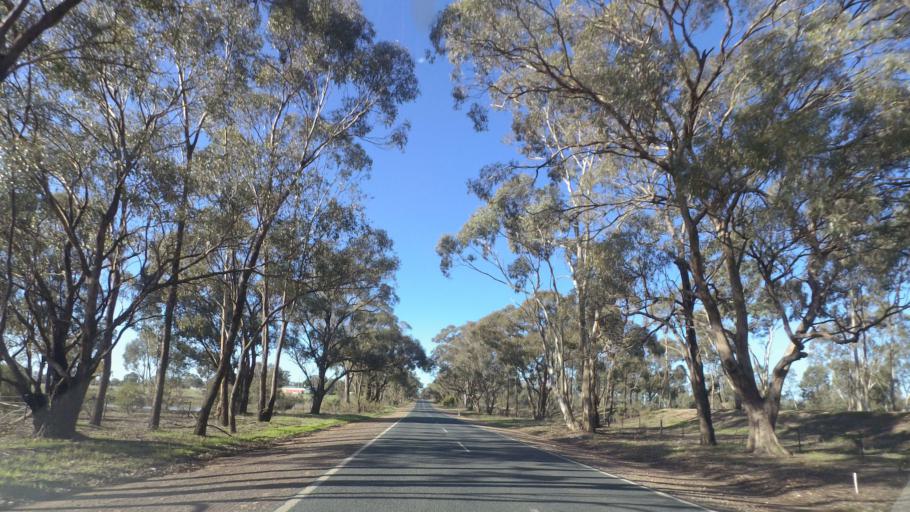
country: AU
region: Victoria
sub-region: Greater Bendigo
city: Epsom
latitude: -36.6776
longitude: 144.3854
